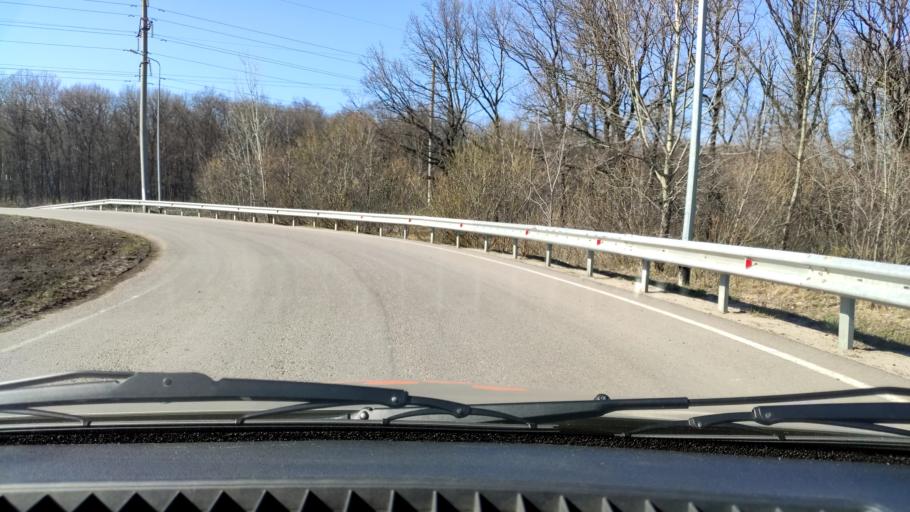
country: RU
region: Voronezj
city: Somovo
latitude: 51.6868
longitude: 39.3420
